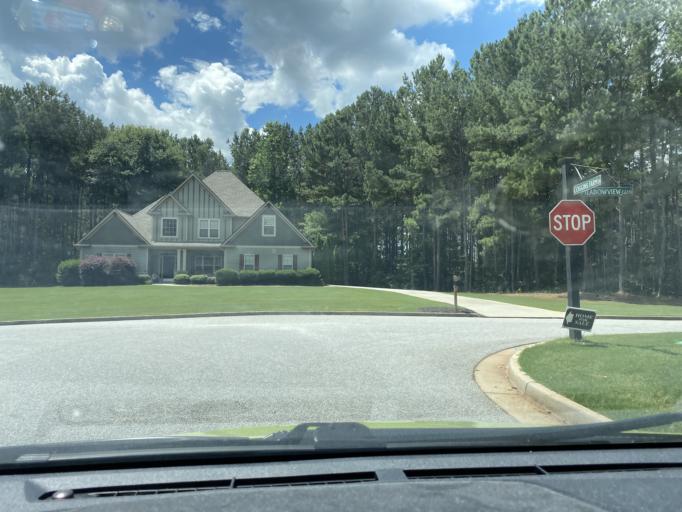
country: US
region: Georgia
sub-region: Fayette County
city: Peachtree City
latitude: 33.4300
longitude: -84.6758
